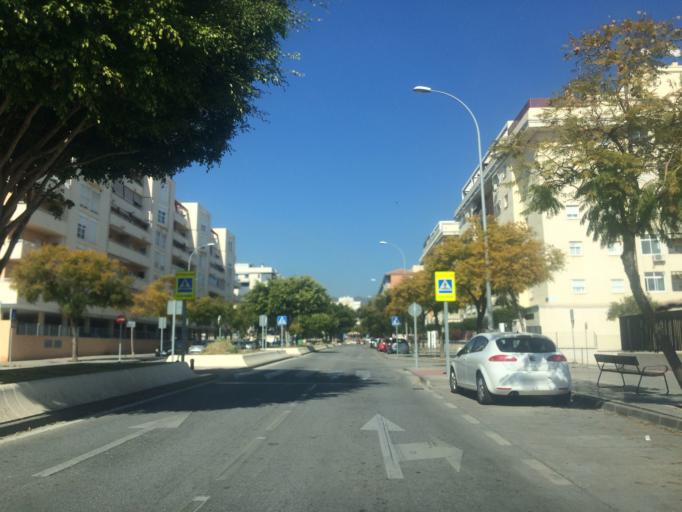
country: ES
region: Andalusia
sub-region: Provincia de Malaga
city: Malaga
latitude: 36.7496
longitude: -4.4270
